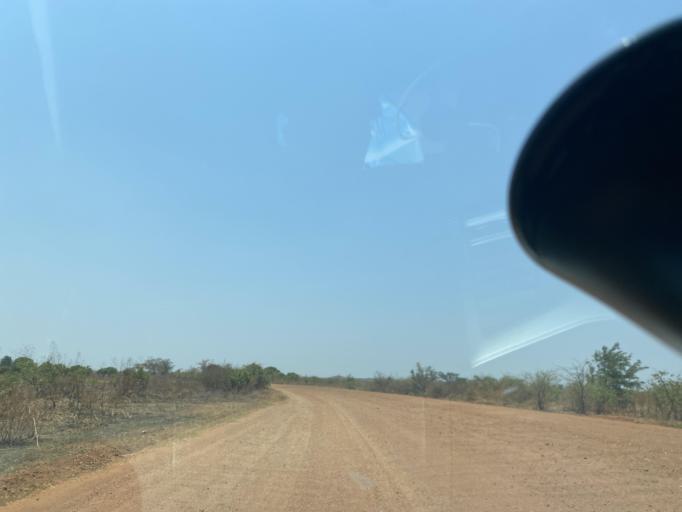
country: ZM
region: Lusaka
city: Lusaka
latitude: -15.4611
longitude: 27.9201
